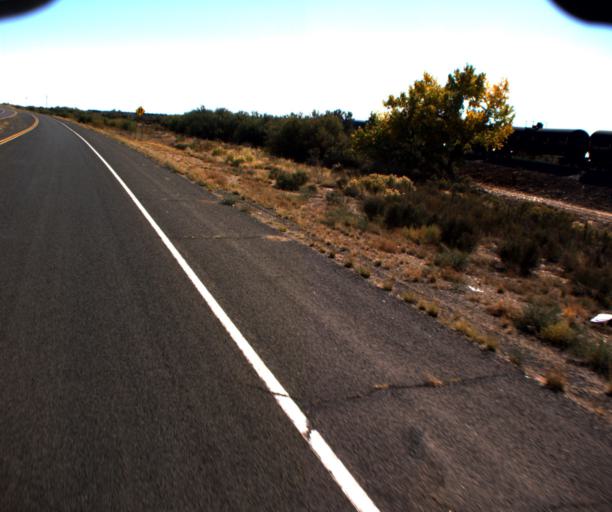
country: US
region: Arizona
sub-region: Navajo County
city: Winslow
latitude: 35.0081
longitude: -110.6615
